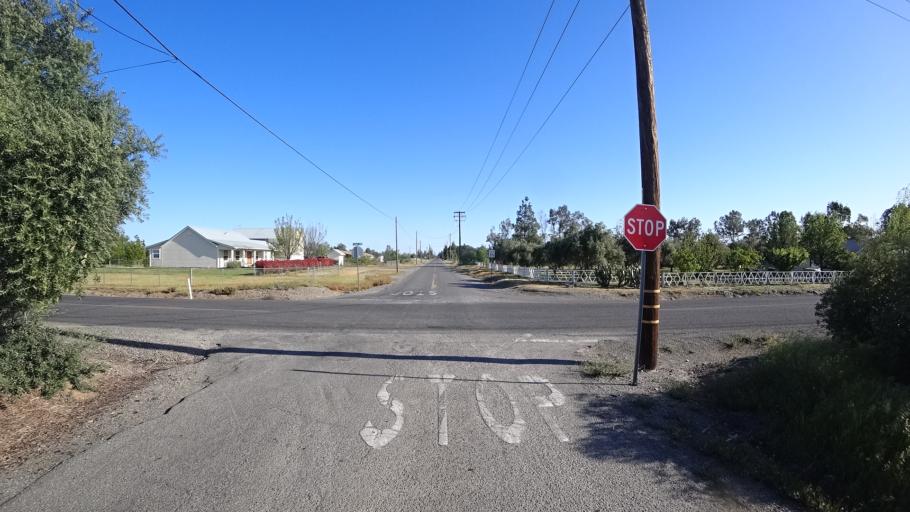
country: US
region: California
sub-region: Glenn County
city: Orland
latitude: 39.7254
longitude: -122.1878
